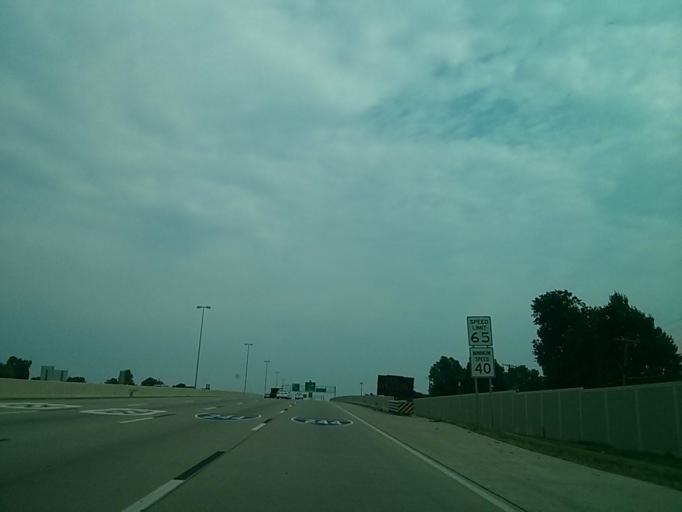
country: US
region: Oklahoma
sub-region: Tulsa County
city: Owasso
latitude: 36.1536
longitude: -95.8604
